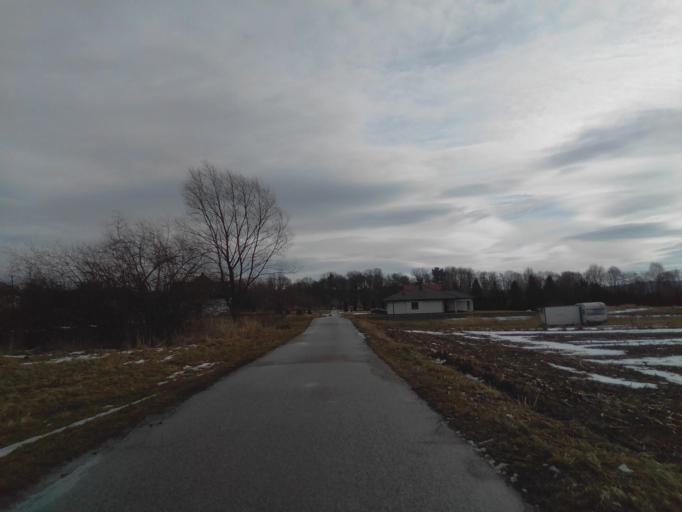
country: PL
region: Subcarpathian Voivodeship
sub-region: Powiat przemyski
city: Nienadowa
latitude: 49.8179
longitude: 22.4110
